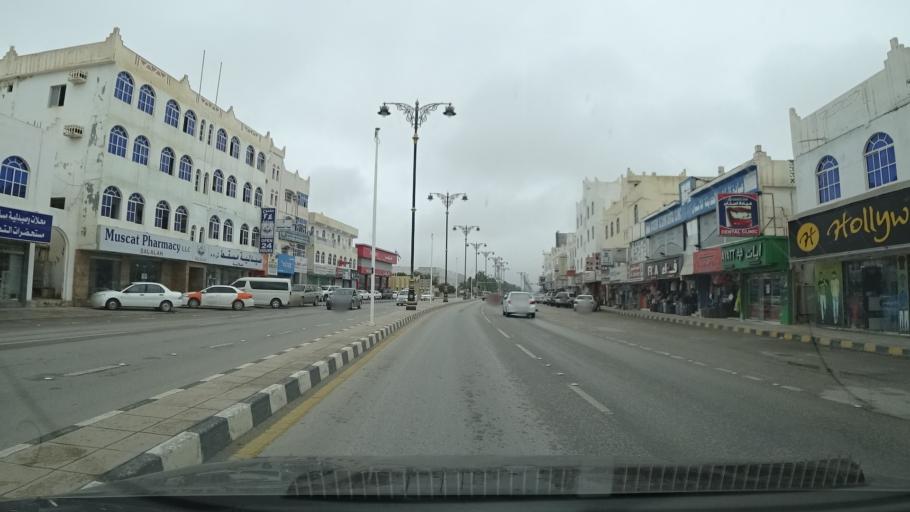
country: OM
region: Zufar
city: Salalah
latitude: 17.0133
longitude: 54.0936
